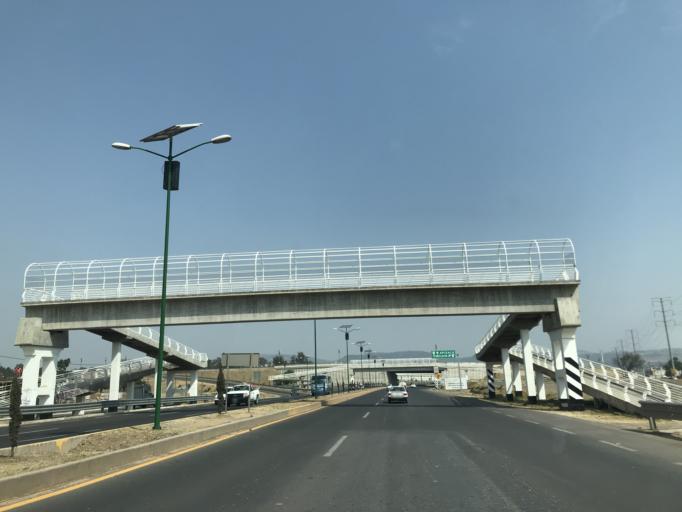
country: MX
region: Tlaxcala
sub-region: Chiautempan
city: Santa Cruz Tetela
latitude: 19.3018
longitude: -98.1975
